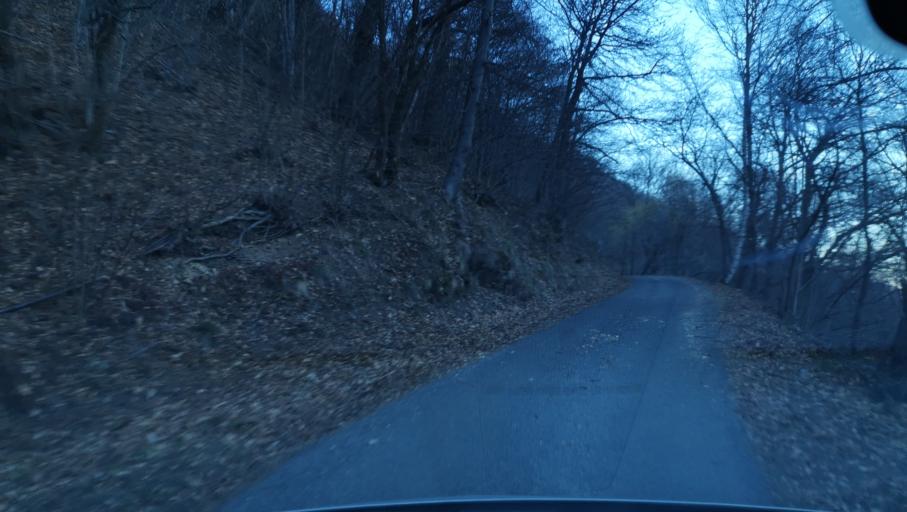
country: IT
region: Piedmont
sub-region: Provincia di Torino
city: Rora
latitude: 44.7760
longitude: 7.1976
